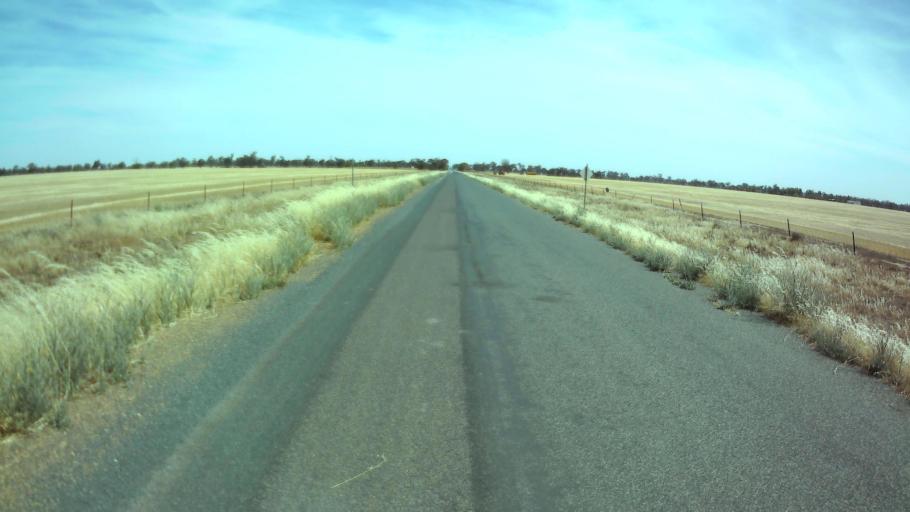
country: AU
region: New South Wales
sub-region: Weddin
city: Grenfell
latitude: -33.9859
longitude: 147.7770
